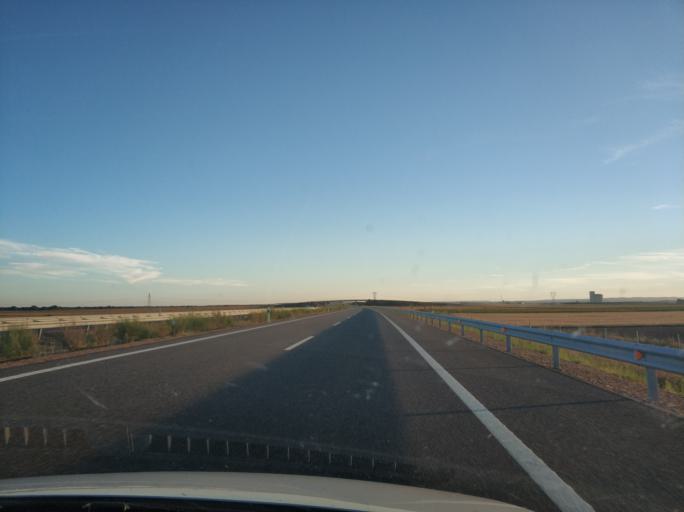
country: ES
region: Castille and Leon
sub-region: Provincia de Zamora
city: Barcial del Barco
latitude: 41.9441
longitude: -5.6348
